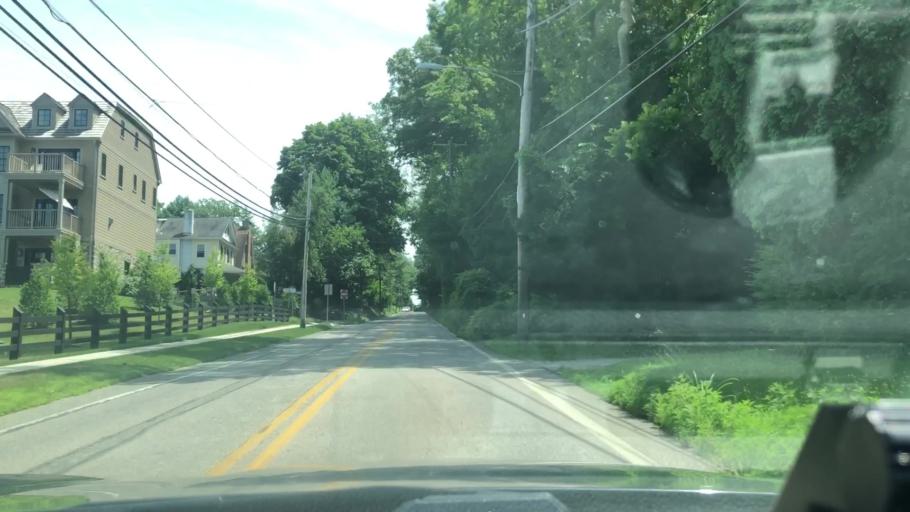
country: US
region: Pennsylvania
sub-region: Montgomery County
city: Flourtown
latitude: 40.0905
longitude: -75.2196
